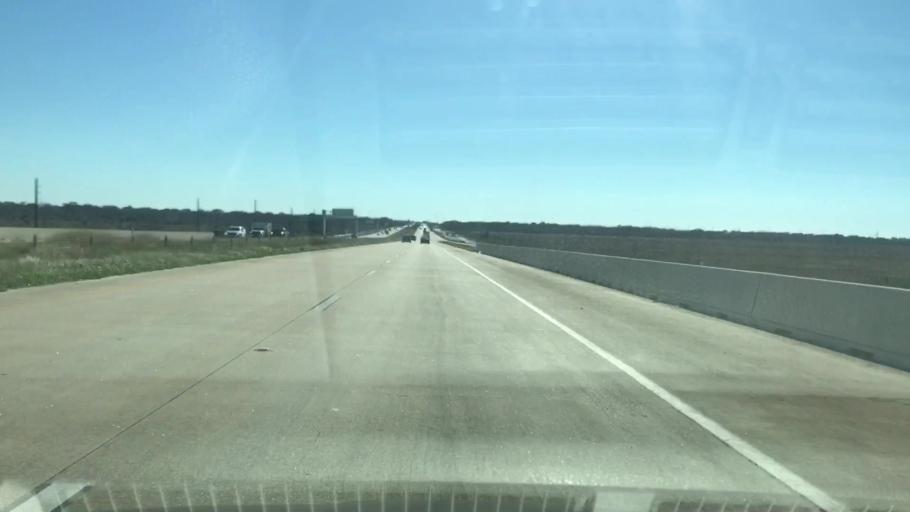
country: US
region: Texas
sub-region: Harris County
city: Cypress
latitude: 29.9770
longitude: -95.7697
